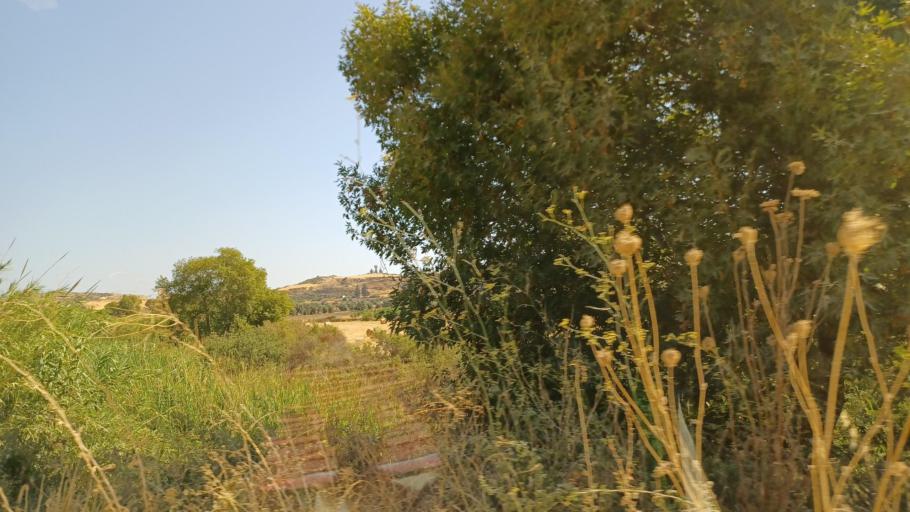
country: CY
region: Pafos
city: Polis
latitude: 35.0049
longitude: 32.4308
